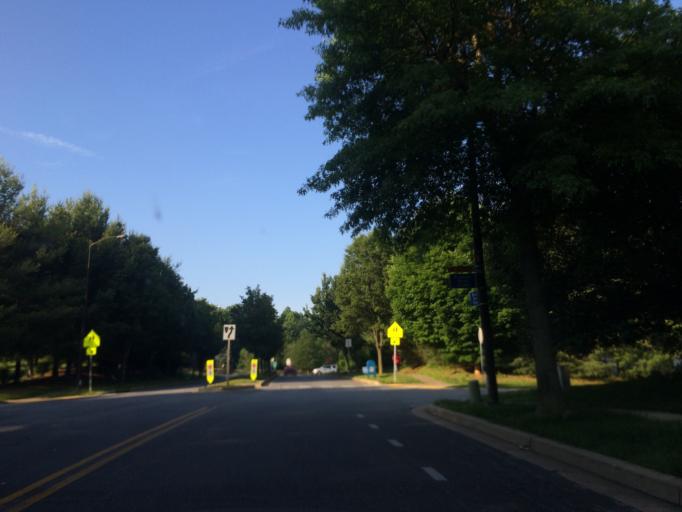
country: US
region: Maryland
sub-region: Howard County
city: Highland
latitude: 39.1921
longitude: -76.9287
